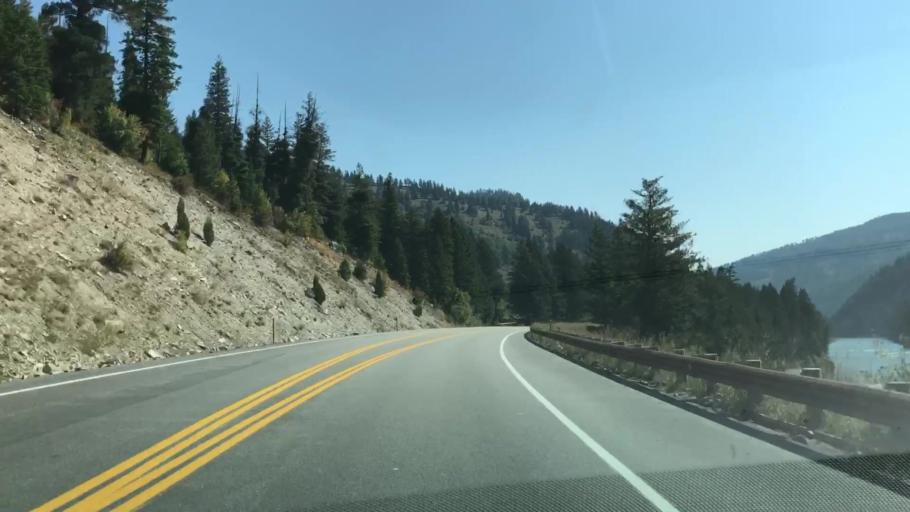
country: US
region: Wyoming
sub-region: Teton County
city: Hoback
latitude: 43.1982
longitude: -110.9060
